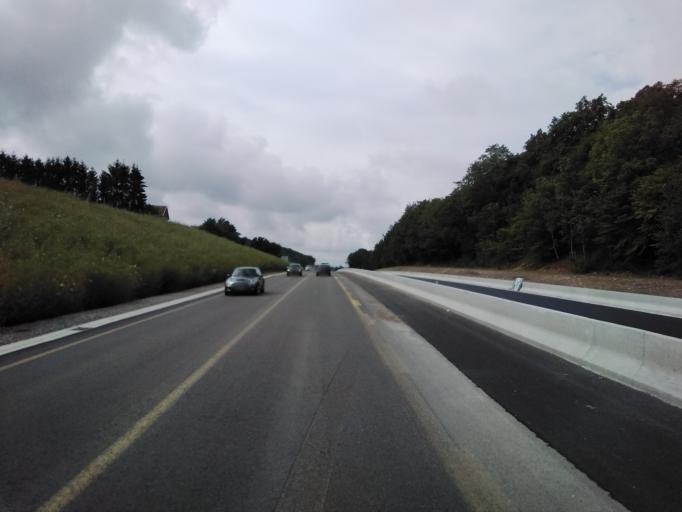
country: FR
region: Franche-Comte
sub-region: Departement du Doubs
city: Chatillon-le-Duc
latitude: 47.3009
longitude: 5.9889
